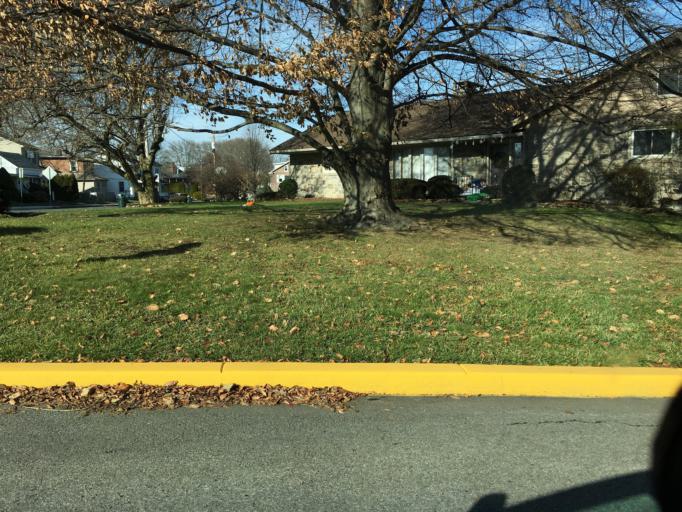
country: US
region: Pennsylvania
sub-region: Berks County
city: Kutztown
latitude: 40.5127
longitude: -75.7788
